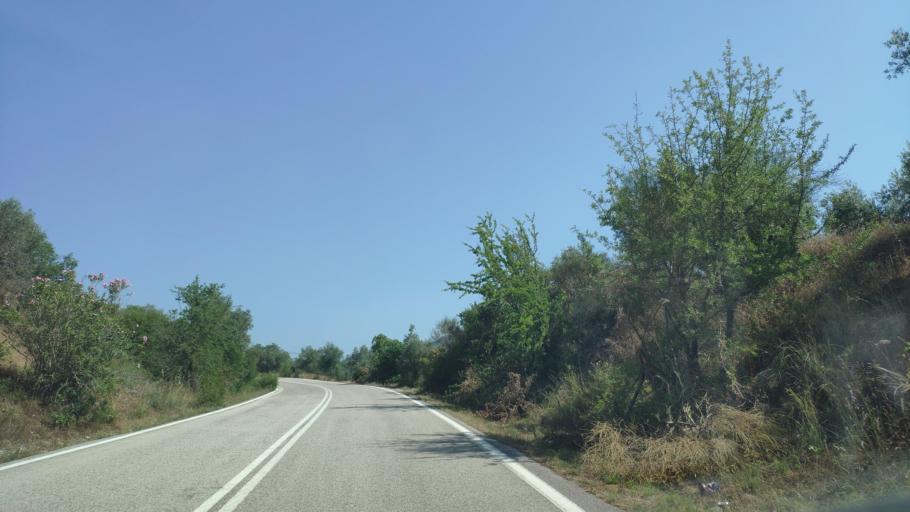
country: GR
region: West Greece
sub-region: Nomos Aitolias kai Akarnanias
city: Lepenou
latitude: 38.7485
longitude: 21.3432
